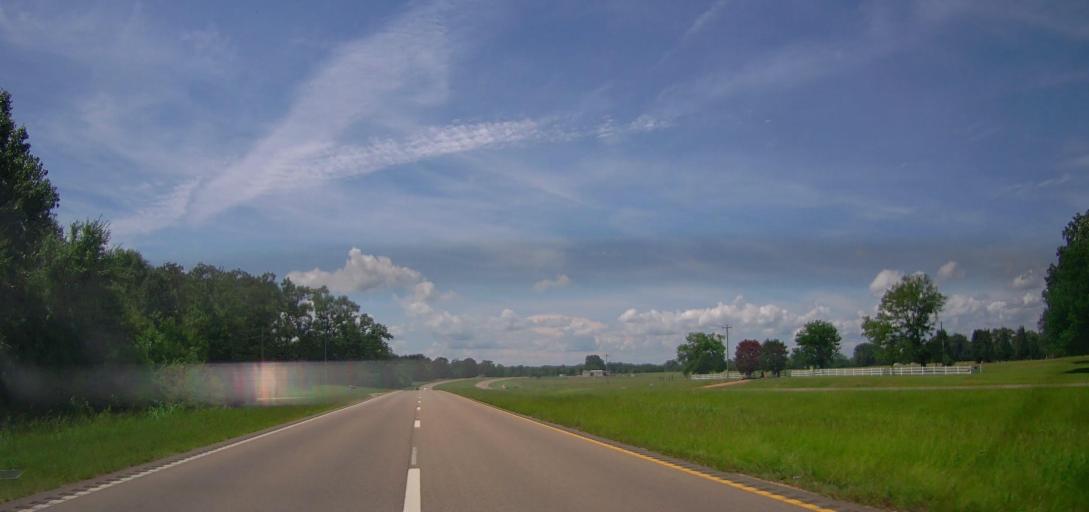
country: US
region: Mississippi
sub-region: Monroe County
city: Amory
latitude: 33.9575
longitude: -88.6089
